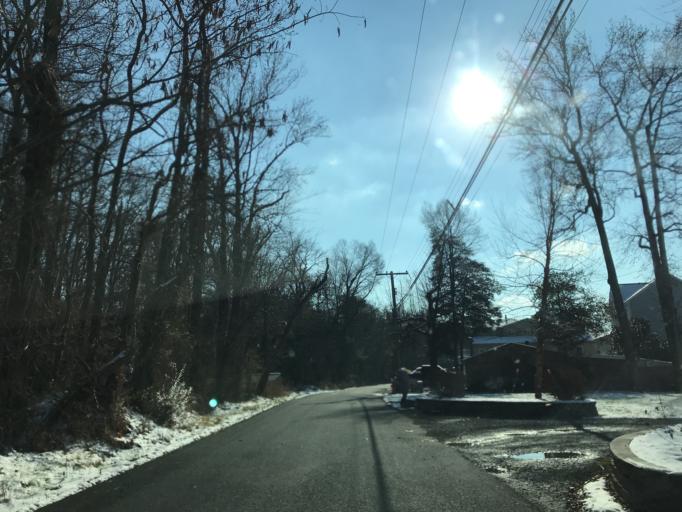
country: US
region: Maryland
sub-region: Baltimore County
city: Bowleys Quarters
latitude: 39.3066
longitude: -76.3795
